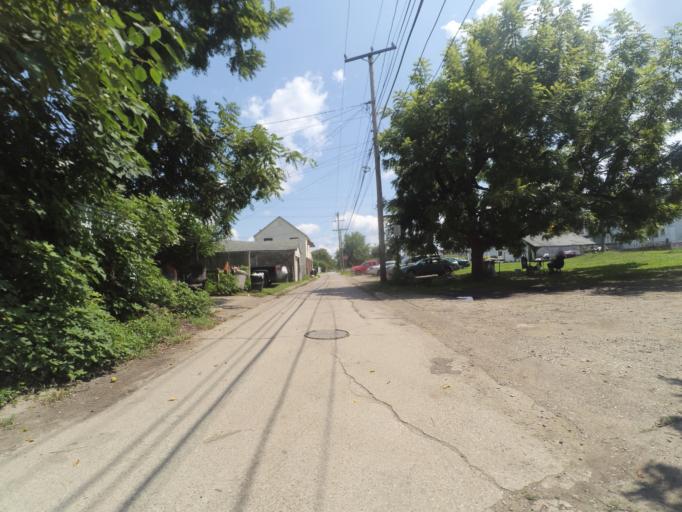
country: US
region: West Virginia
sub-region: Cabell County
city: Huntington
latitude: 38.4160
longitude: -82.4615
